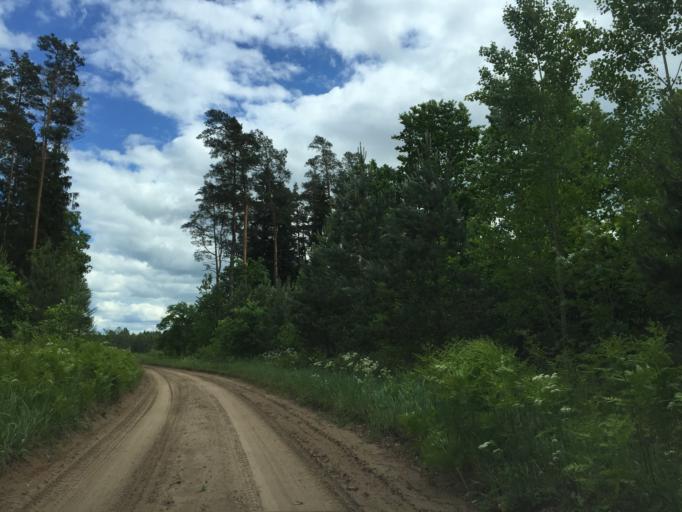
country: LV
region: Lecava
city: Iecava
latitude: 56.5669
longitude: 24.3024
